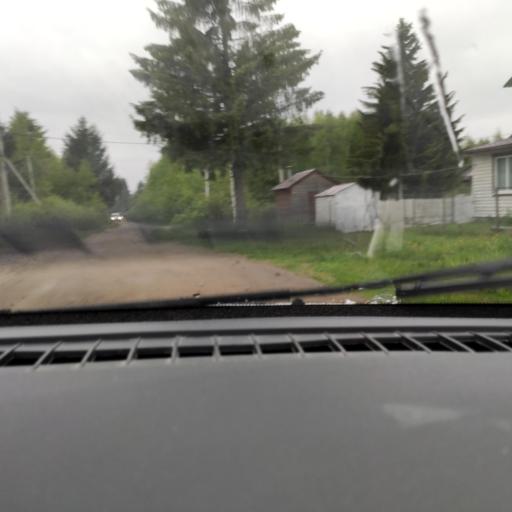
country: RU
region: Perm
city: Kondratovo
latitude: 58.0510
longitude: 56.0188
